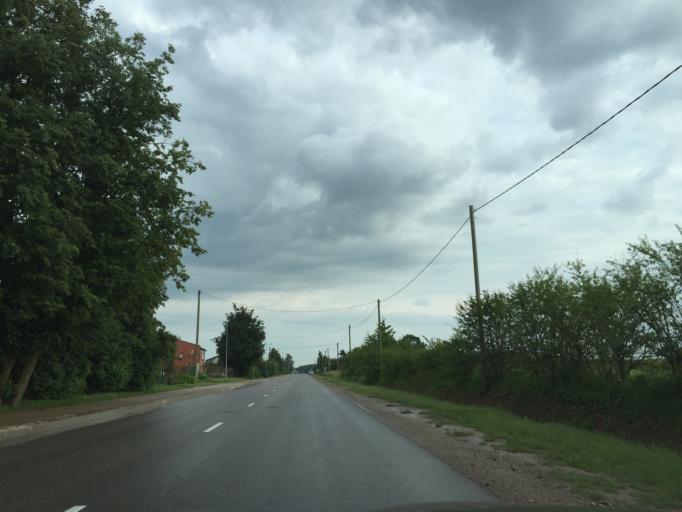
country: LV
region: Dobeles Rajons
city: Dobele
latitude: 56.6147
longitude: 23.2731
